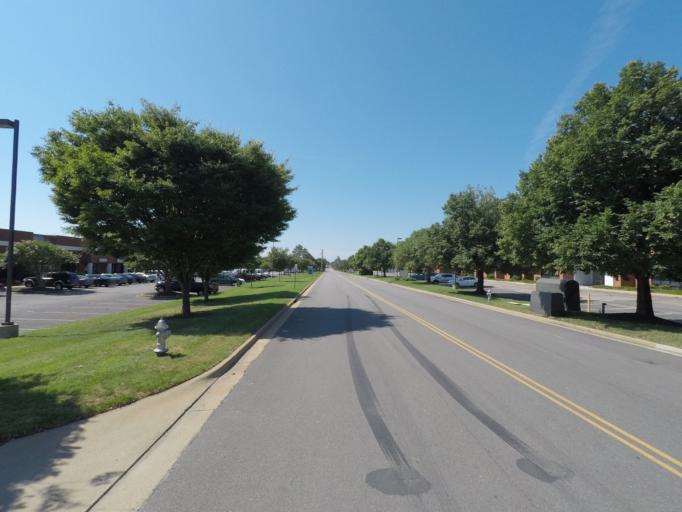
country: US
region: Virginia
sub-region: Henrico County
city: Dumbarton
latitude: 37.5825
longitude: -77.4793
